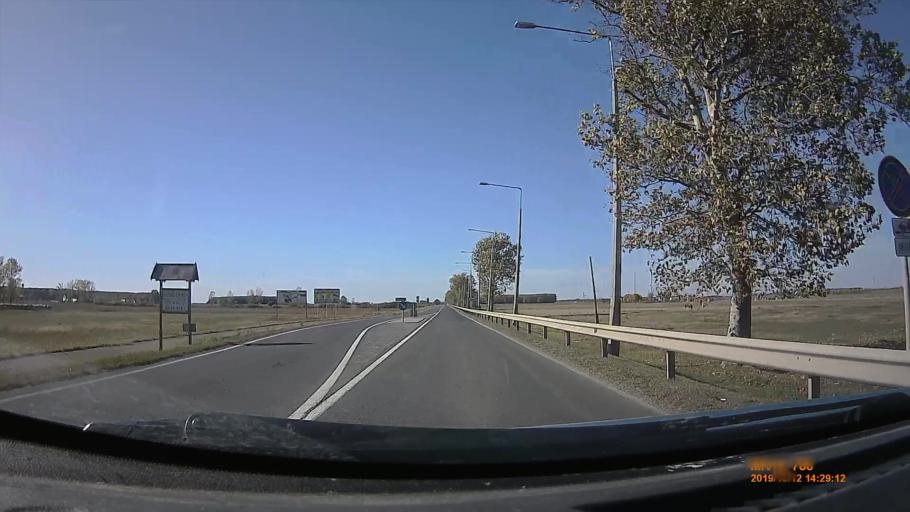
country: HU
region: Hajdu-Bihar
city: Berettyoujfalu
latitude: 47.1691
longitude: 21.6163
